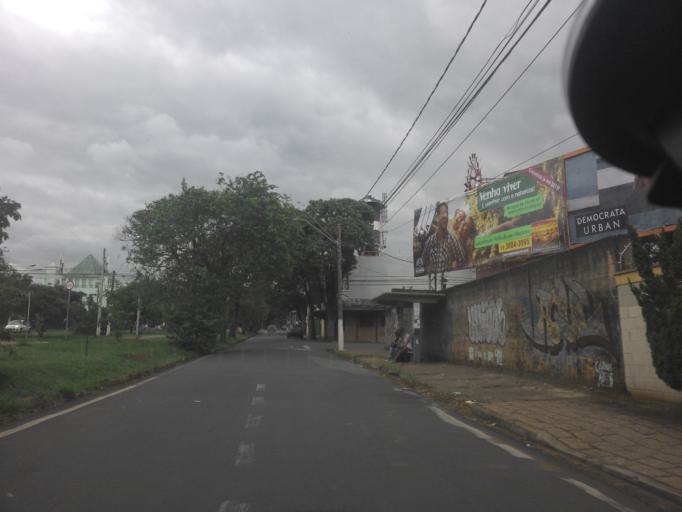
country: BR
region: Sao Paulo
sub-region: Campinas
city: Campinas
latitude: -22.8183
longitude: -47.0730
